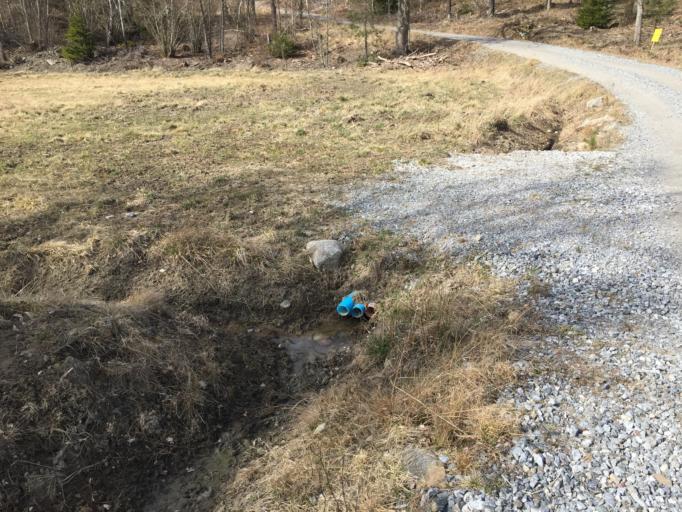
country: SE
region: Stockholm
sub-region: Salems Kommun
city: Ronninge
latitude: 59.2518
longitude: 17.6844
